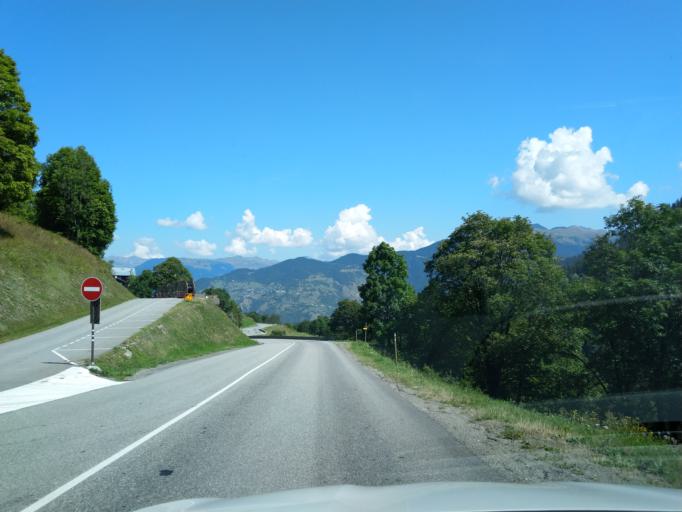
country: FR
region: Rhone-Alpes
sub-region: Departement de la Savoie
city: Meribel
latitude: 45.4162
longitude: 6.5552
